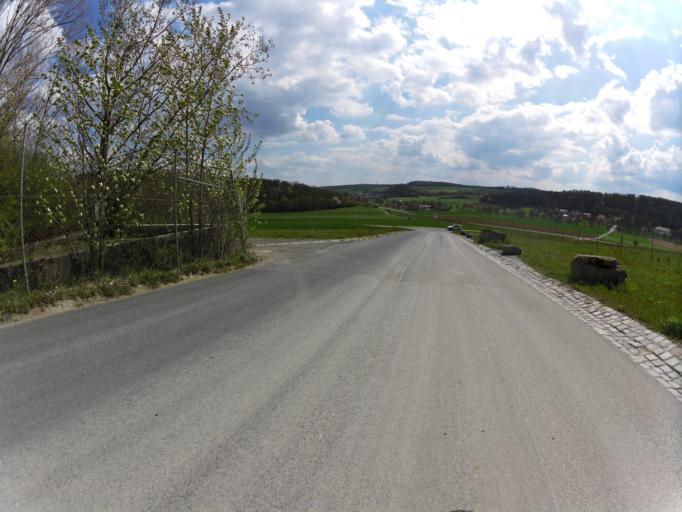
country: DE
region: Bavaria
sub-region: Regierungsbezirk Unterfranken
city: Greussenheim
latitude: 49.7964
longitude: 9.7679
